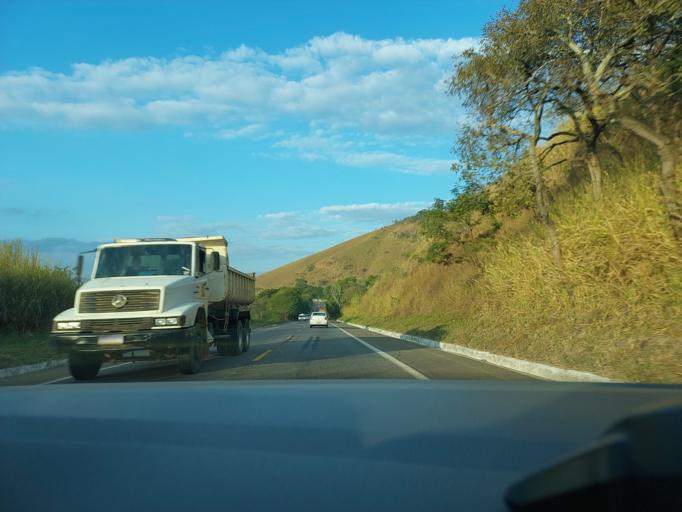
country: BR
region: Minas Gerais
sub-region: Muriae
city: Muriae
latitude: -21.1270
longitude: -42.2409
